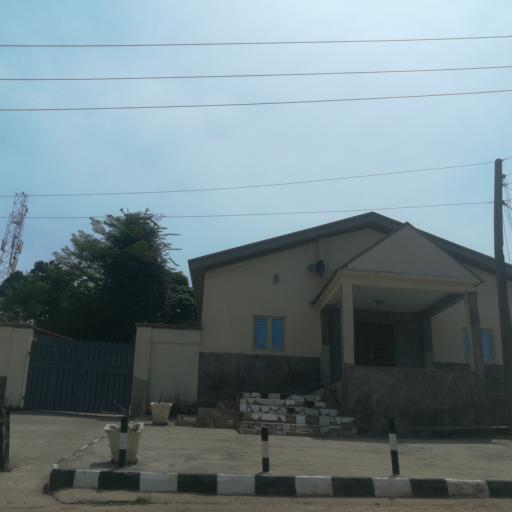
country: NG
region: Plateau
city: Jos
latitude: 9.9044
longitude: 8.8714
